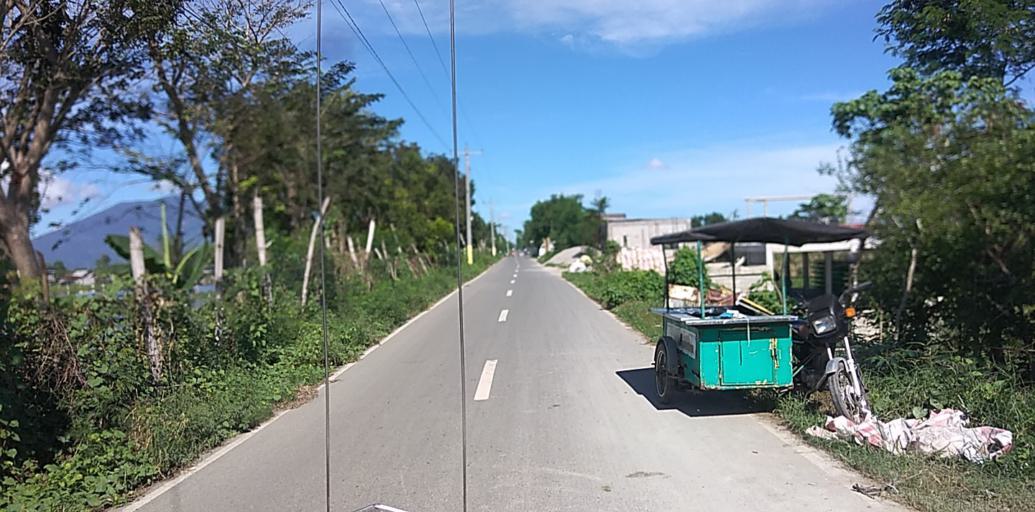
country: PH
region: Central Luzon
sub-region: Province of Pampanga
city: Candaba
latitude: 15.1115
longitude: 120.8162
